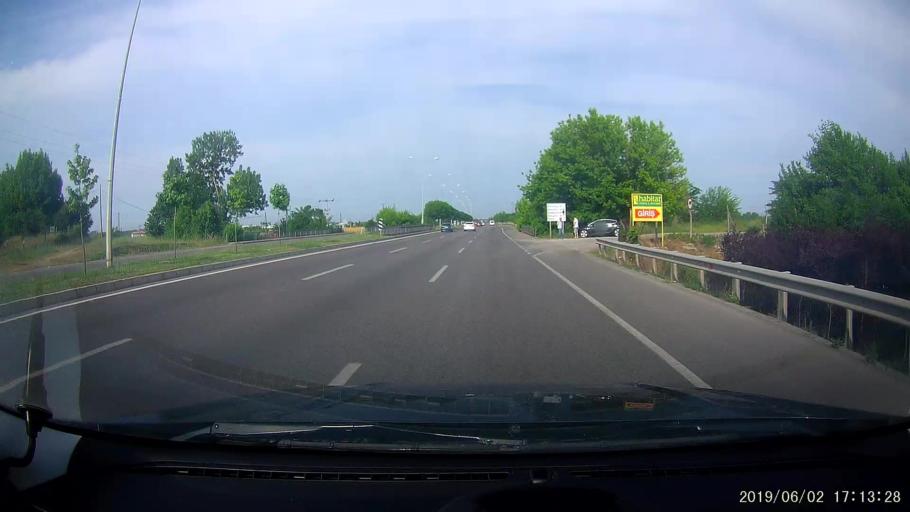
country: TR
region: Samsun
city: Tekkekoy
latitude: 41.2313
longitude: 36.5090
